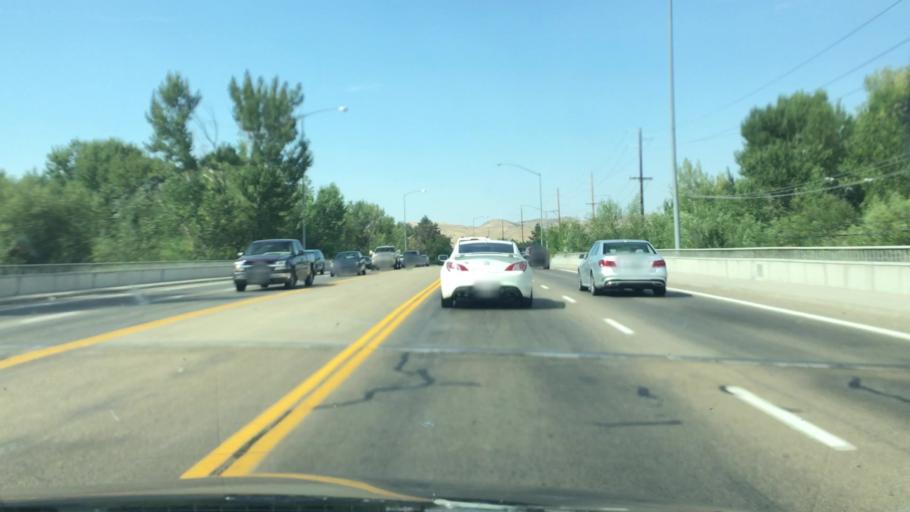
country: US
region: Idaho
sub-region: Ada County
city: Garden City
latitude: 43.6608
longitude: -116.2797
